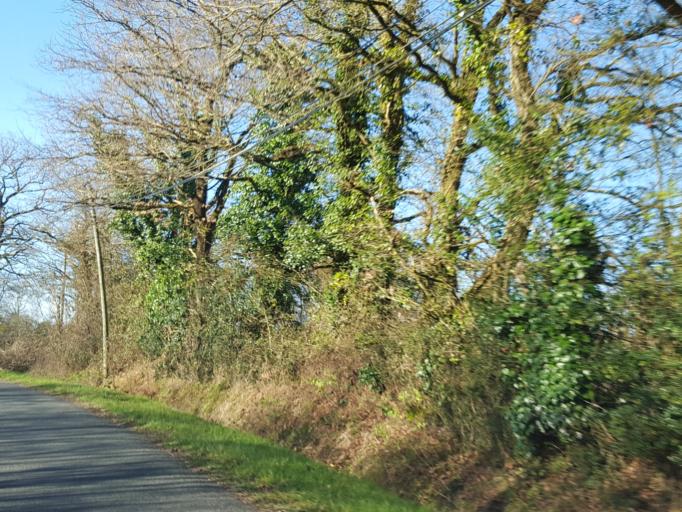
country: FR
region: Pays de la Loire
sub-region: Departement de la Vendee
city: Venansault
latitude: 46.6829
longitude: -1.5015
